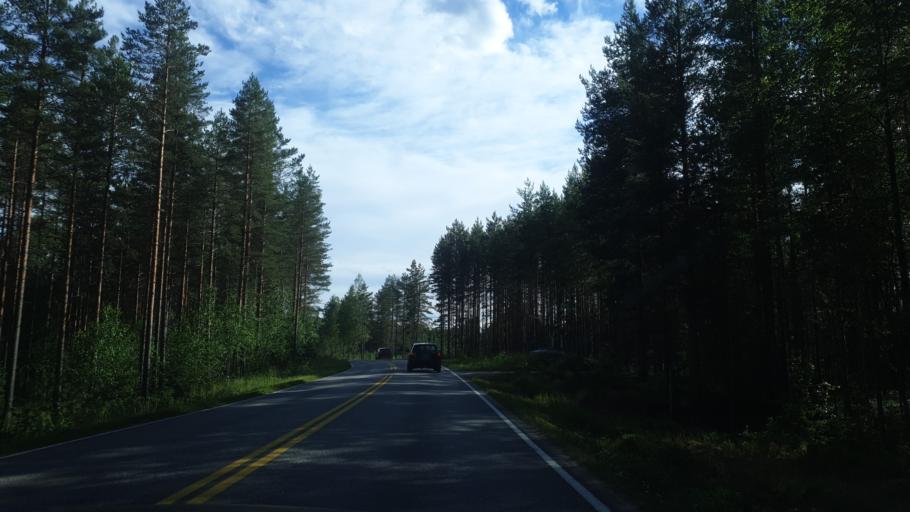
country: FI
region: Southern Savonia
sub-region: Mikkeli
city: Pertunmaa
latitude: 61.4856
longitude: 26.4663
